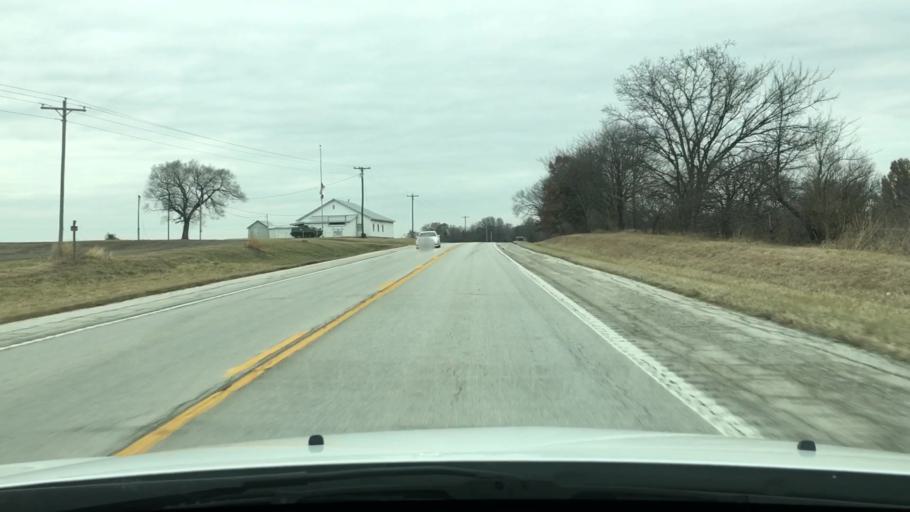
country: US
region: Missouri
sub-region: Montgomery County
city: Wellsville
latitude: 39.2042
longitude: -91.6465
